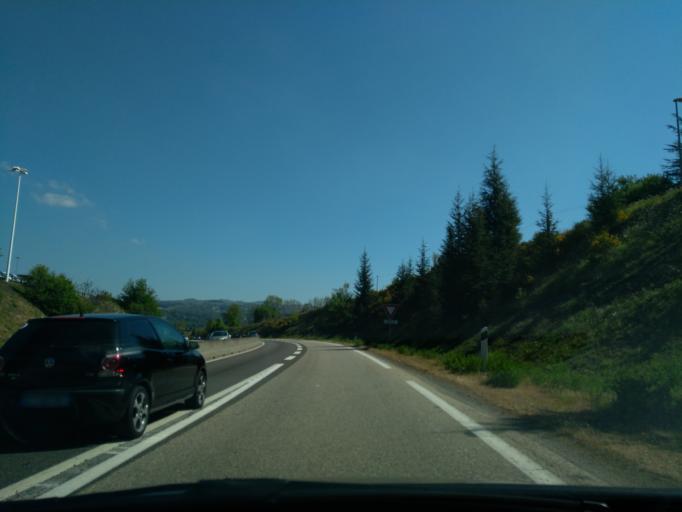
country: FR
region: Rhone-Alpes
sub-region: Departement de la Loire
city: Villars
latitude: 45.4668
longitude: 4.3428
